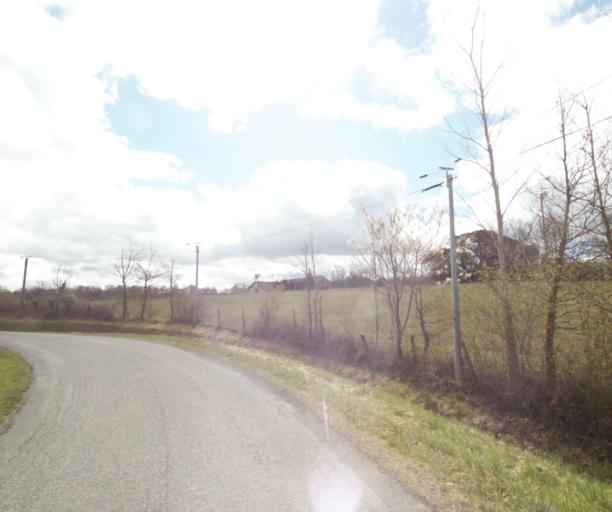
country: FR
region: Midi-Pyrenees
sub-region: Departement de l'Ariege
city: Saverdun
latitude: 43.2053
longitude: 1.5753
